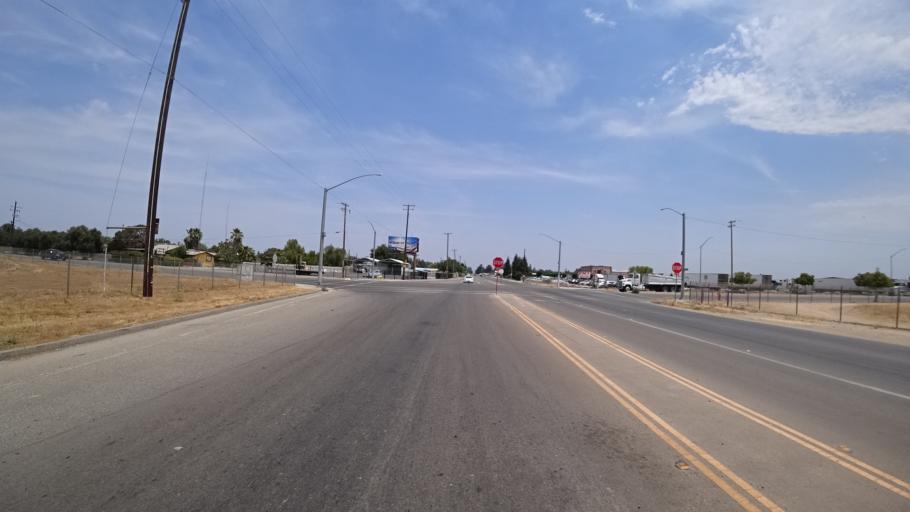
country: US
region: California
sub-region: Fresno County
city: West Park
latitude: 36.7502
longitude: -119.8449
